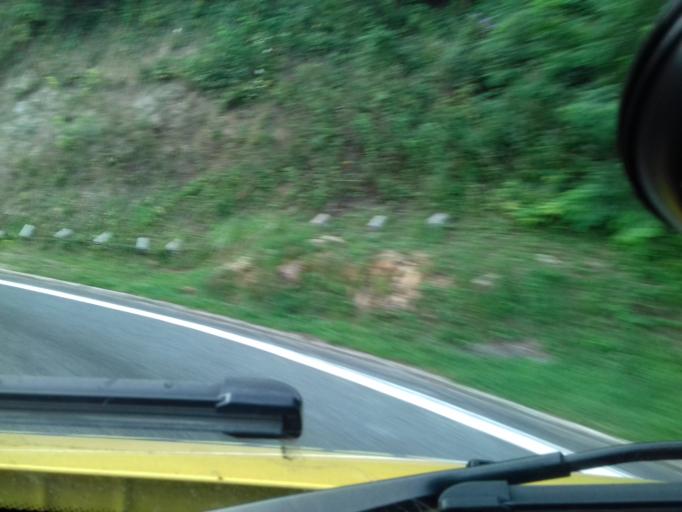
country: BA
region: Federation of Bosnia and Herzegovina
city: Ostrozac
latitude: 44.9045
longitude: 15.9398
